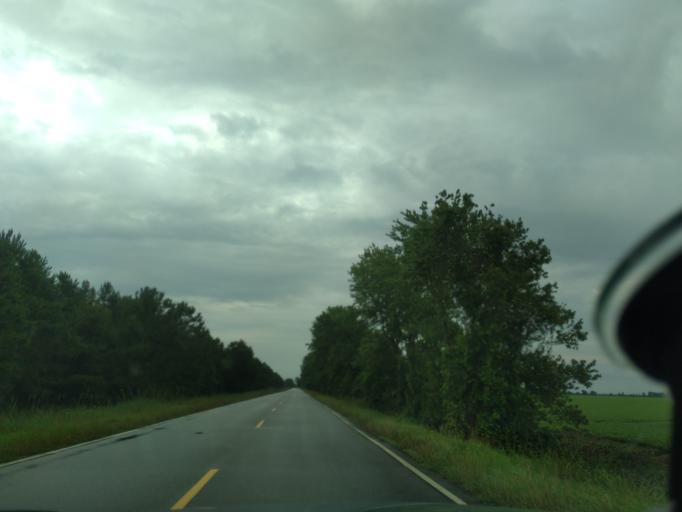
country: US
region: North Carolina
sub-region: Washington County
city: Plymouth
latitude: 35.8477
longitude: -76.5590
